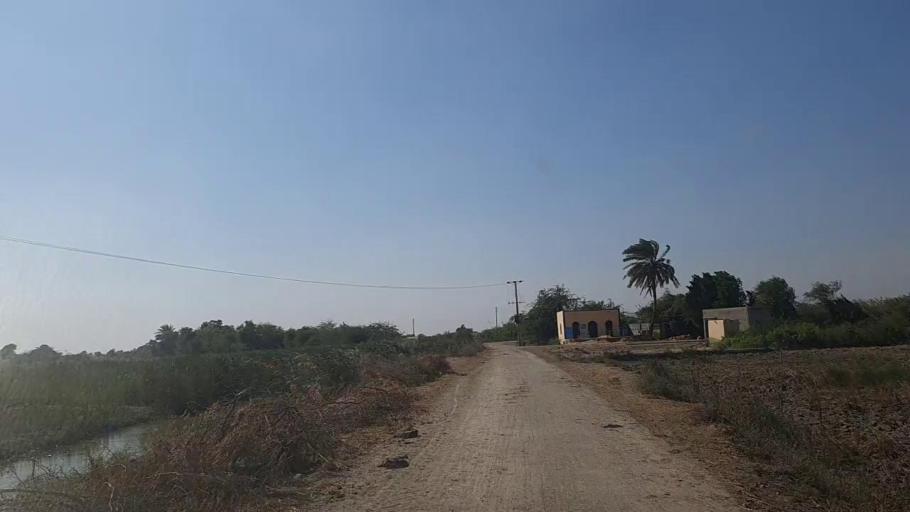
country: PK
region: Sindh
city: Daro Mehar
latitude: 24.9738
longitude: 68.1249
